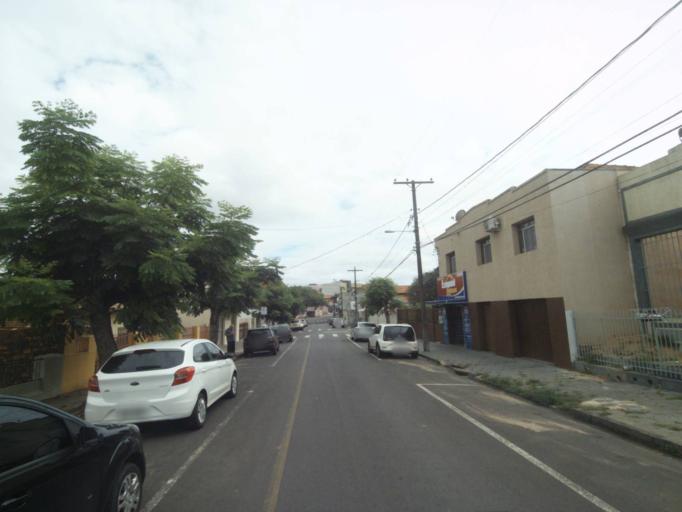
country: BR
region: Parana
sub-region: Telemaco Borba
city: Telemaco Borba
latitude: -24.3227
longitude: -50.6186
